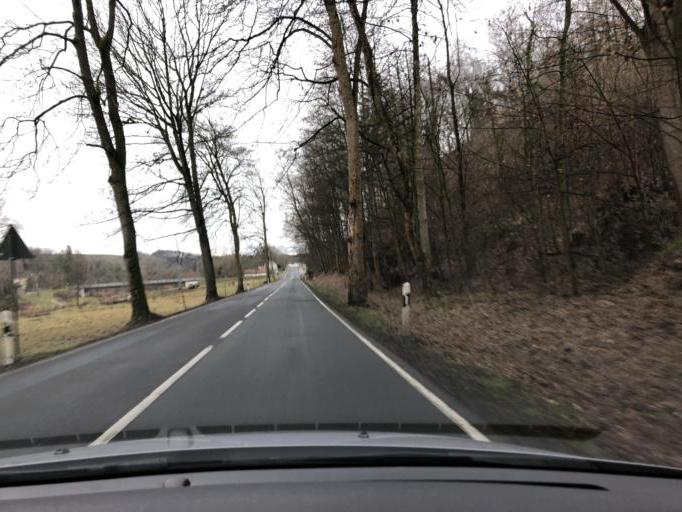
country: DE
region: Saxony
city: Niederstriegis
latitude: 51.0879
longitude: 13.1365
